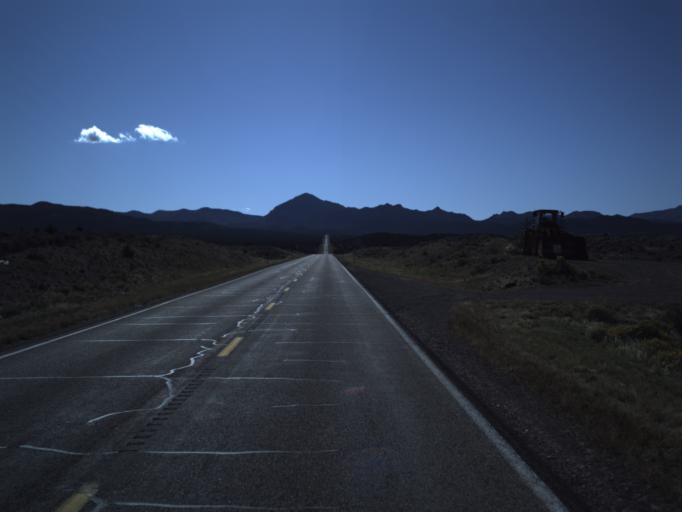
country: US
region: Utah
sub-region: Washington County
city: Enterprise
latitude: 37.6559
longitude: -113.4557
